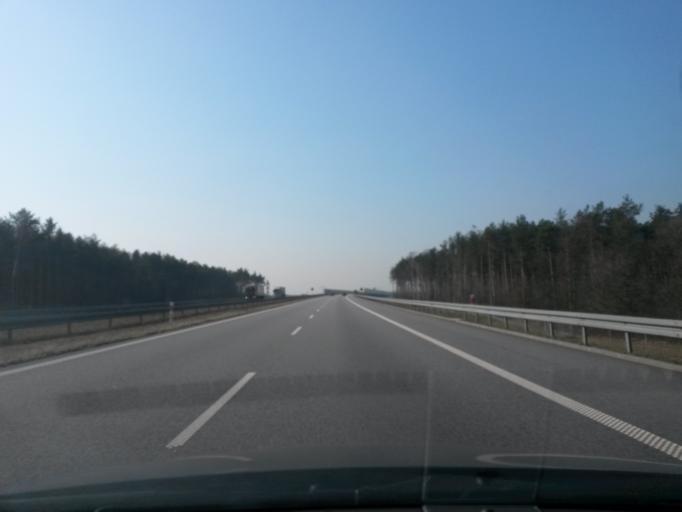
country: PL
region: Lodz Voivodeship
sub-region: powiat Lowicki
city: Domaniewice
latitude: 51.9542
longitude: 19.8434
